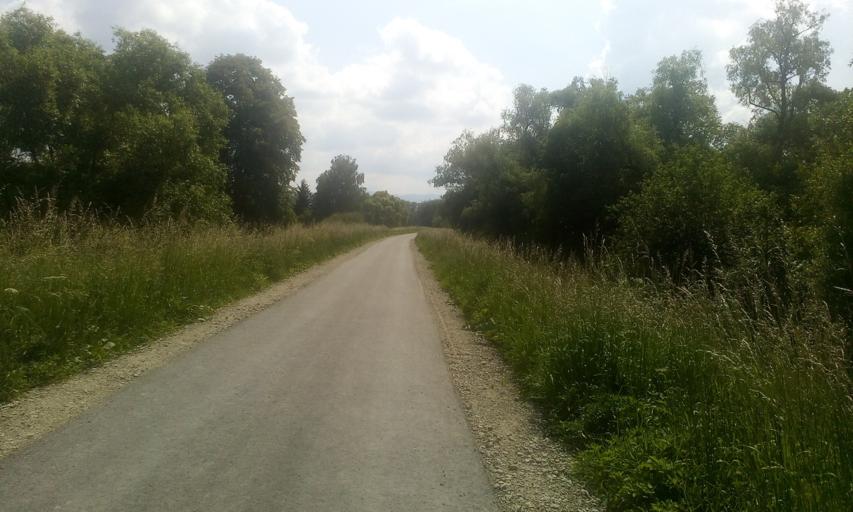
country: PL
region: Lesser Poland Voivodeship
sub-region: Powiat nowosadecki
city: Nowy Sacz
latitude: 49.6150
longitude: 20.6829
